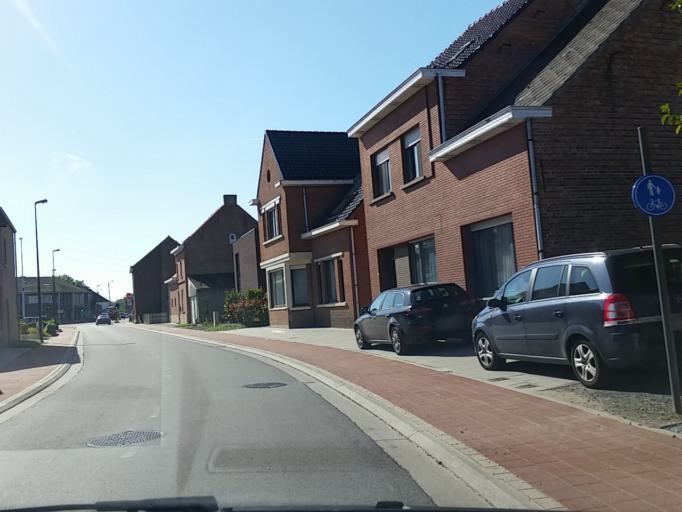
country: BE
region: Flanders
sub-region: Provincie Vlaams-Brabant
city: Kampenhout
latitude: 50.9446
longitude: 4.5644
